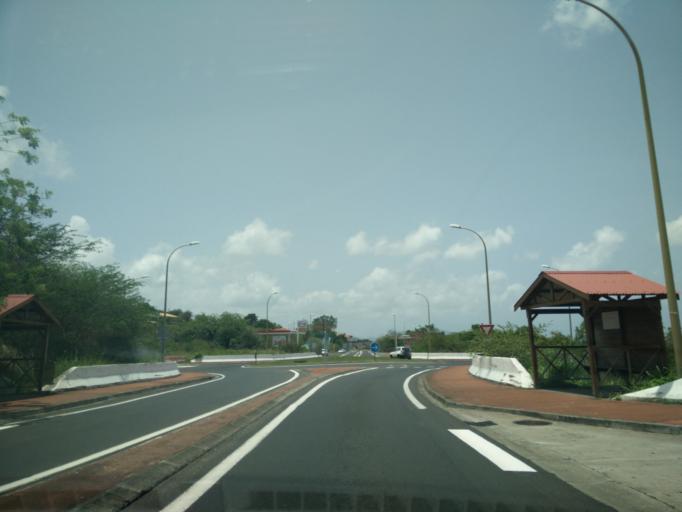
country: MQ
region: Martinique
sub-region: Martinique
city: Fort-de-France
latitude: 14.6374
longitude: -61.1364
